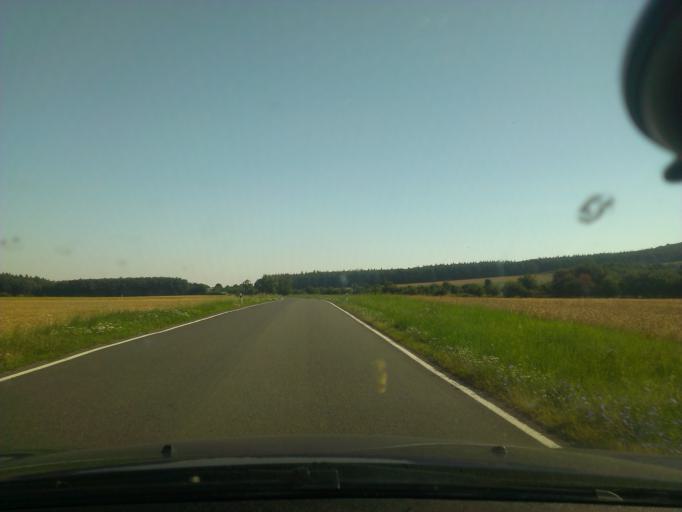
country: CZ
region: South Moravian
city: Velka nad Velickou
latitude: 48.8363
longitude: 17.5184
